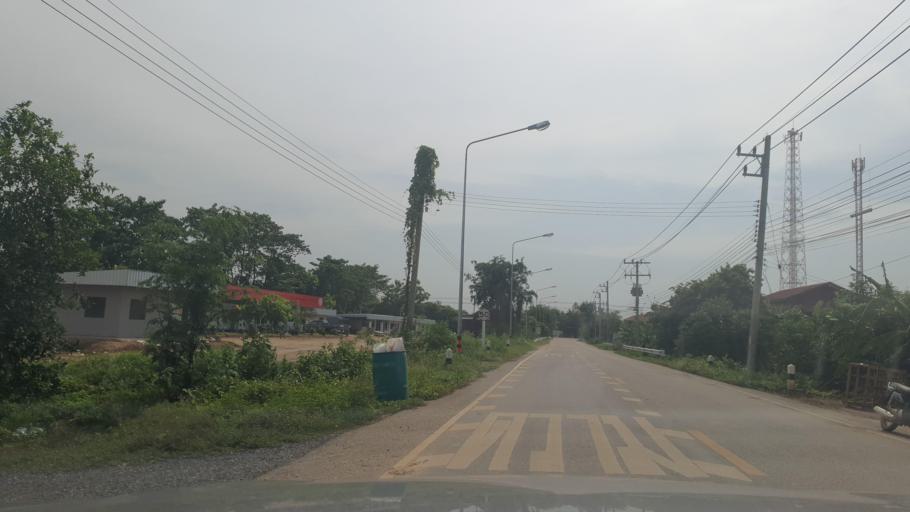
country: TH
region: Sukhothai
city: Si Samrong
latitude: 17.1209
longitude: 99.8533
